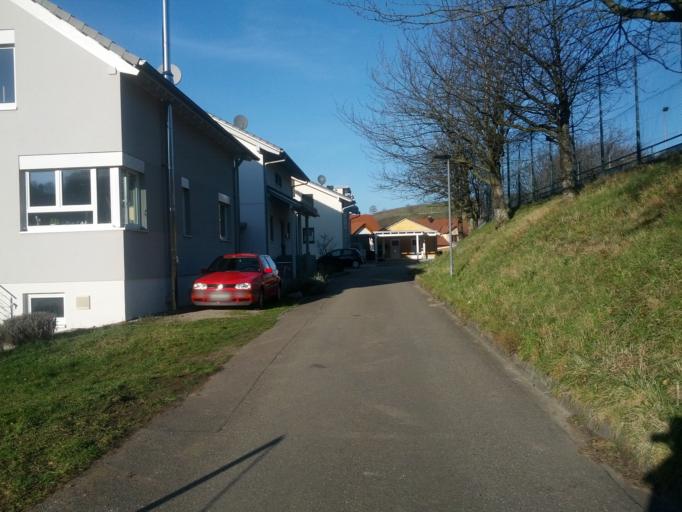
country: DE
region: Baden-Wuerttemberg
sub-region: Freiburg Region
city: Ebringen
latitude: 47.9548
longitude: 7.7749
